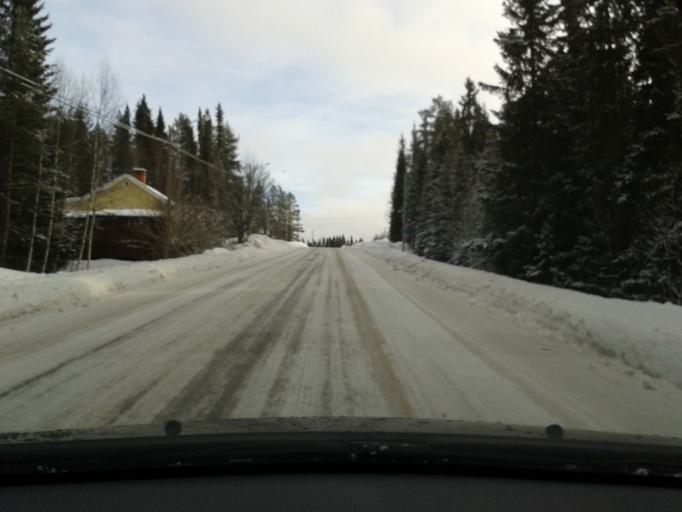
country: SE
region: Vaesterbotten
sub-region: Vilhelmina Kommun
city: Sjoberg
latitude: 64.8007
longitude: 16.0279
